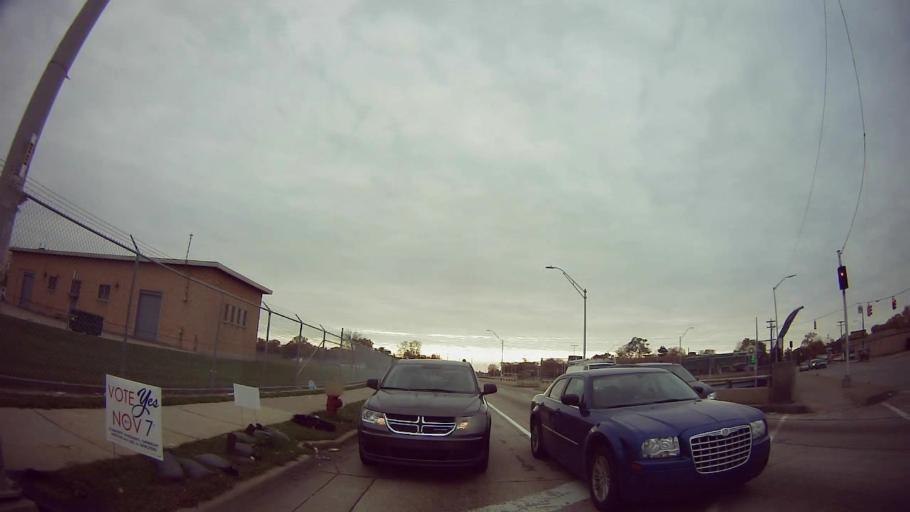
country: US
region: Michigan
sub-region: Oakland County
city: Oak Park
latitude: 42.4426
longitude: -83.2002
